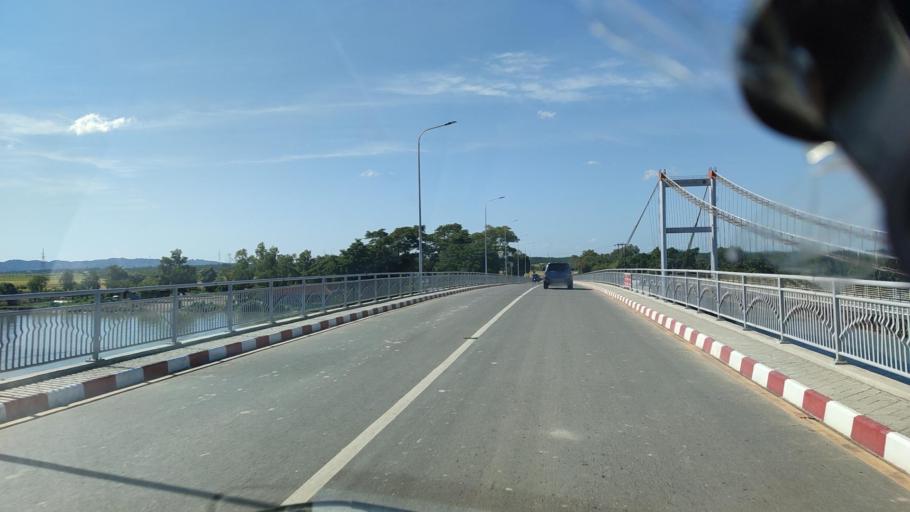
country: MM
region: Rakhine
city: Sittwe
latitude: 20.3992
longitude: 93.3262
